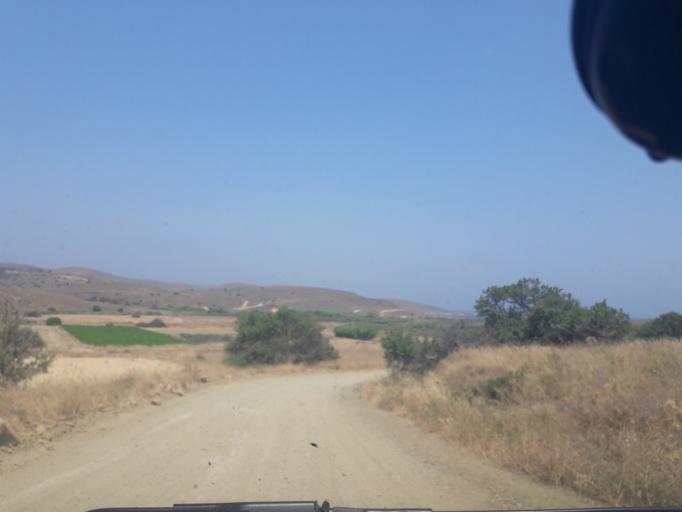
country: GR
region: North Aegean
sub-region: Nomos Lesvou
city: Myrina
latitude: 39.9779
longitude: 25.1500
